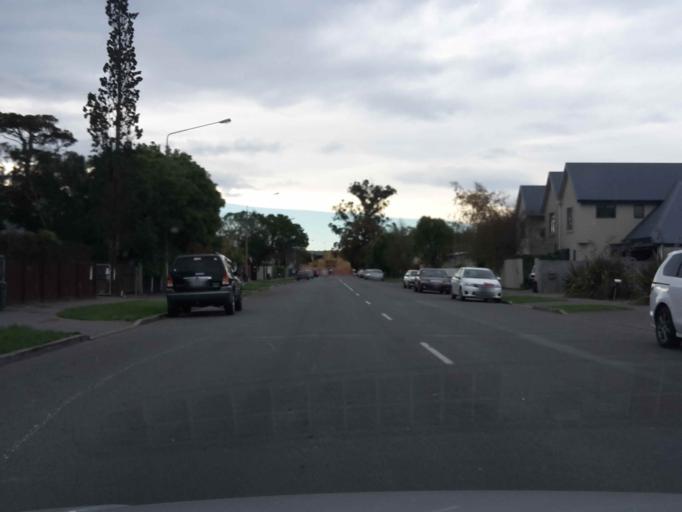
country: NZ
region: Canterbury
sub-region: Christchurch City
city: Christchurch
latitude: -43.5317
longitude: 172.6064
